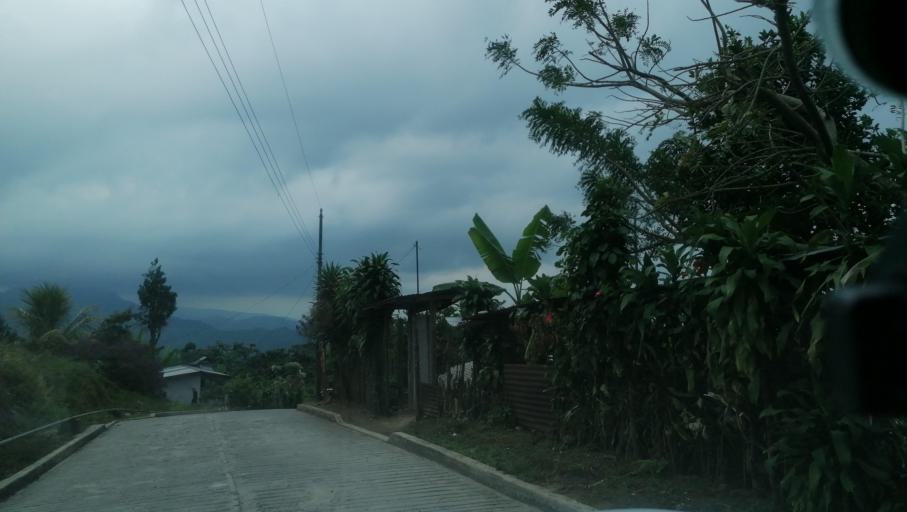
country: MX
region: Chiapas
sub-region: Cacahoatan
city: Benito Juarez
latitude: 15.0790
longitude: -92.1626
